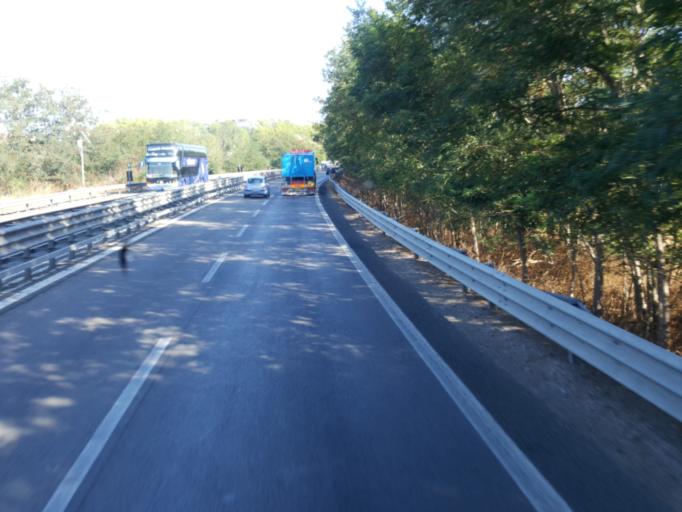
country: IT
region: Latium
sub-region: Provincia di Viterbo
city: Montalto di Castro
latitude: 42.3540
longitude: 11.5963
